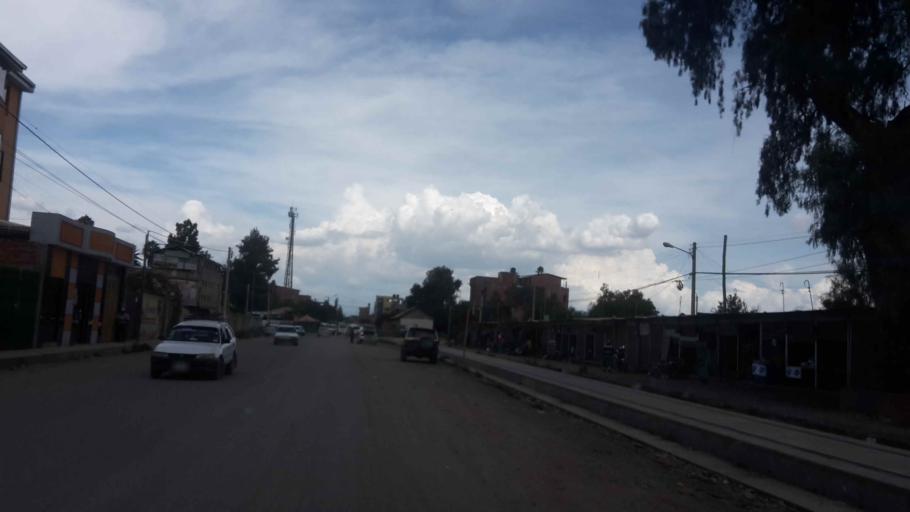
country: BO
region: Cochabamba
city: Sipe Sipe
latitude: -17.4020
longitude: -66.2839
